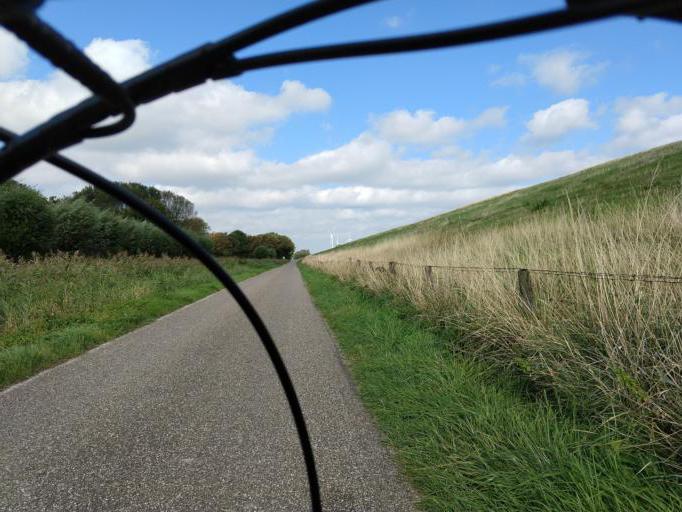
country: NL
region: Zeeland
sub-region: Gemeente Goes
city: Goes
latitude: 51.5752
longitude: 3.8873
